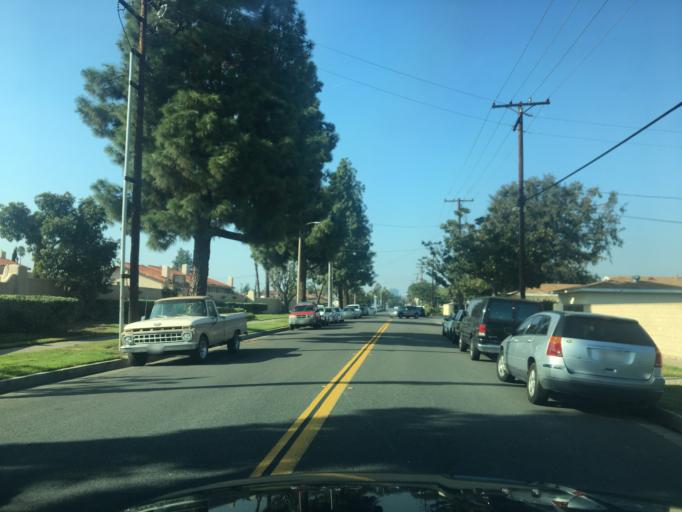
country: US
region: California
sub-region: Orange County
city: Tustin
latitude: 33.7336
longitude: -117.8222
